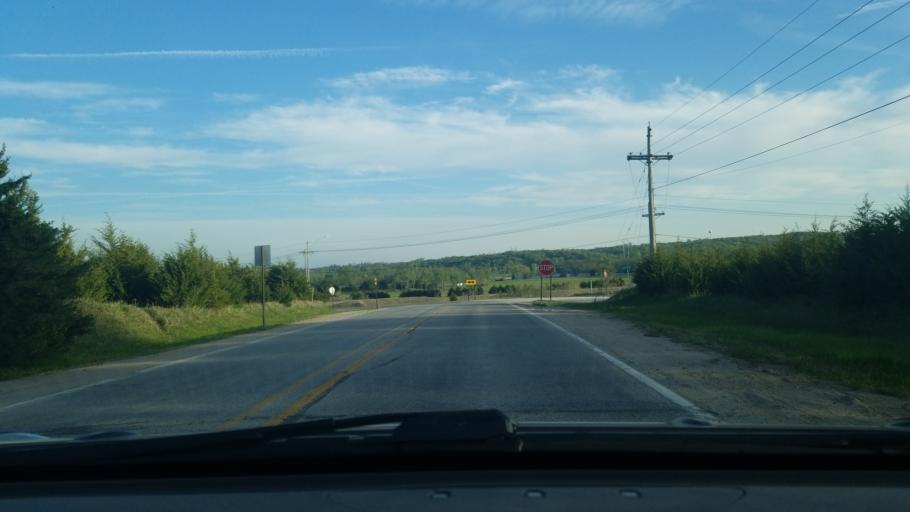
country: US
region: Nebraska
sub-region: Sarpy County
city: Offutt Air Force Base
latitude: 41.0735
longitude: -95.9663
